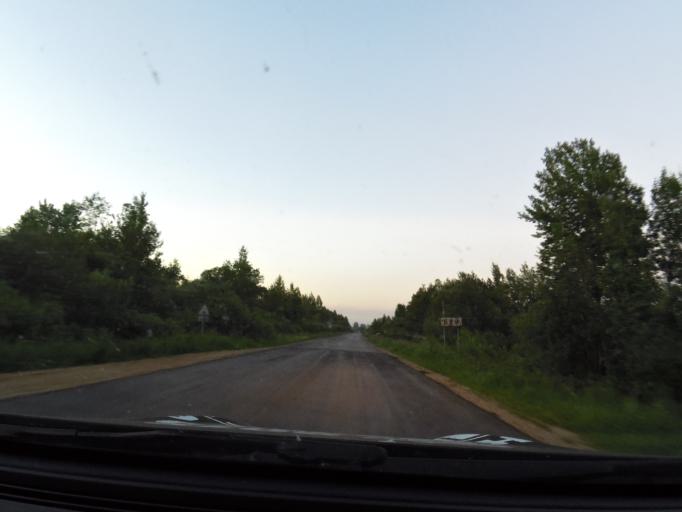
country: RU
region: Kostroma
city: Buy
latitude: 58.4840
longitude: 41.4956
